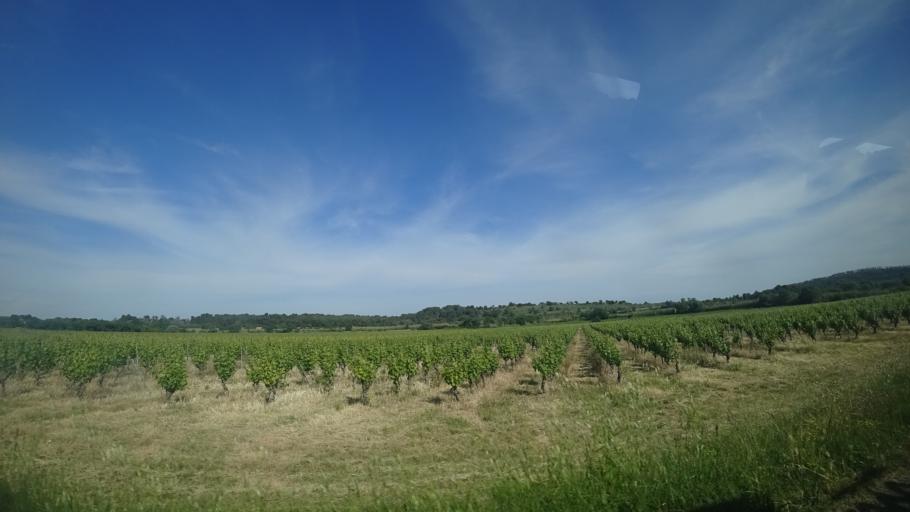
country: FR
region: Languedoc-Roussillon
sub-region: Departement de l'Aude
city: Ginestas
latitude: 43.2795
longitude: 2.8170
